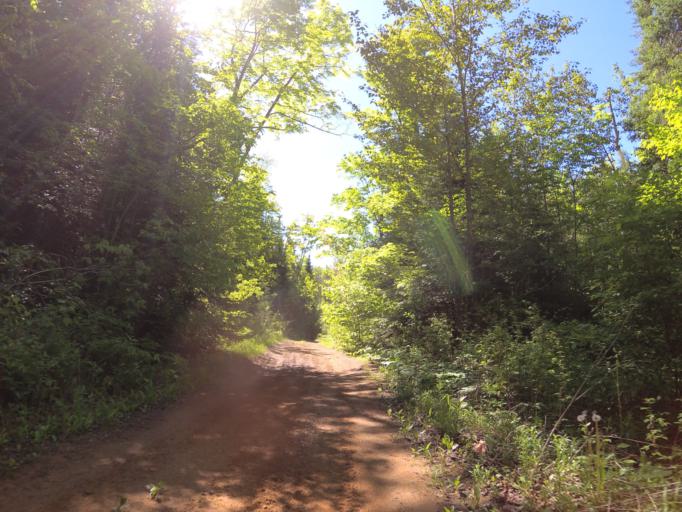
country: CA
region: Ontario
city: Renfrew
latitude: 45.0857
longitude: -77.0920
